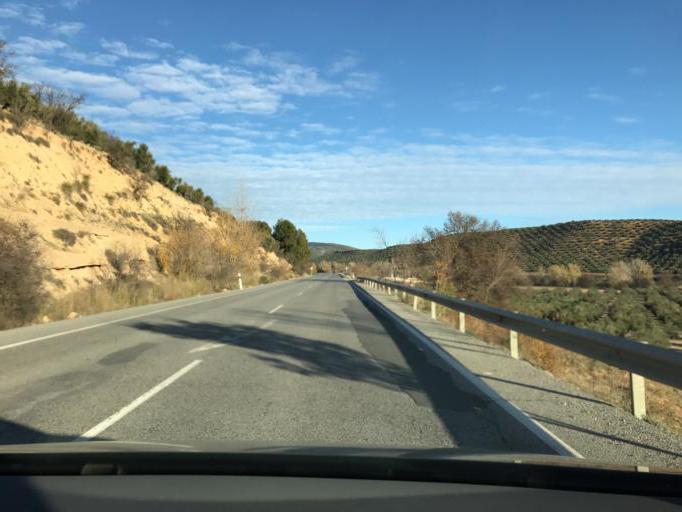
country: ES
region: Andalusia
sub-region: Provincia de Granada
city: Iznalloz
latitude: 37.4037
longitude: -3.5170
